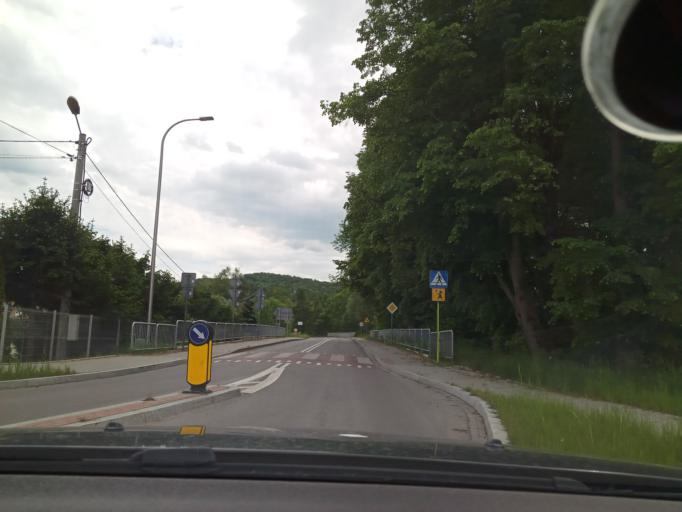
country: PL
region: Lesser Poland Voivodeship
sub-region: Powiat bochenski
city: Lapanow
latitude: 49.8276
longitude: 20.3006
